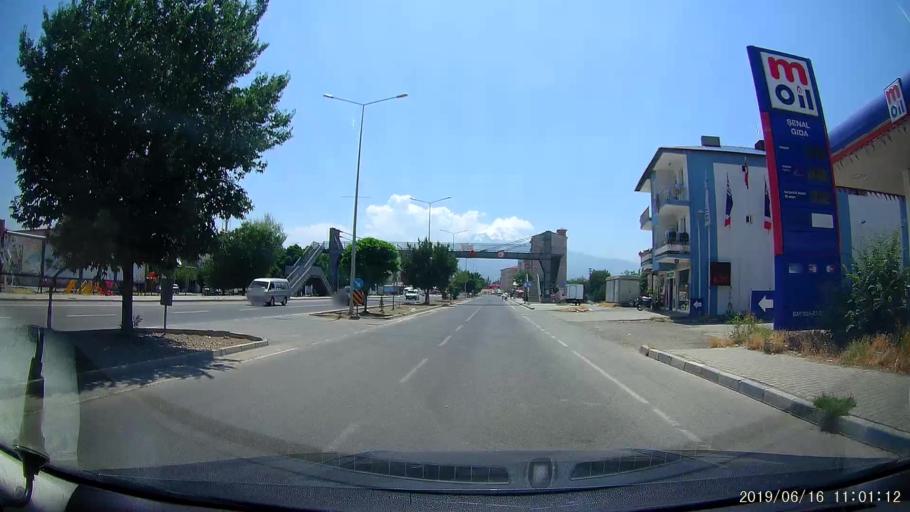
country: TR
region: Igdir
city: Igdir
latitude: 39.9166
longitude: 44.0478
